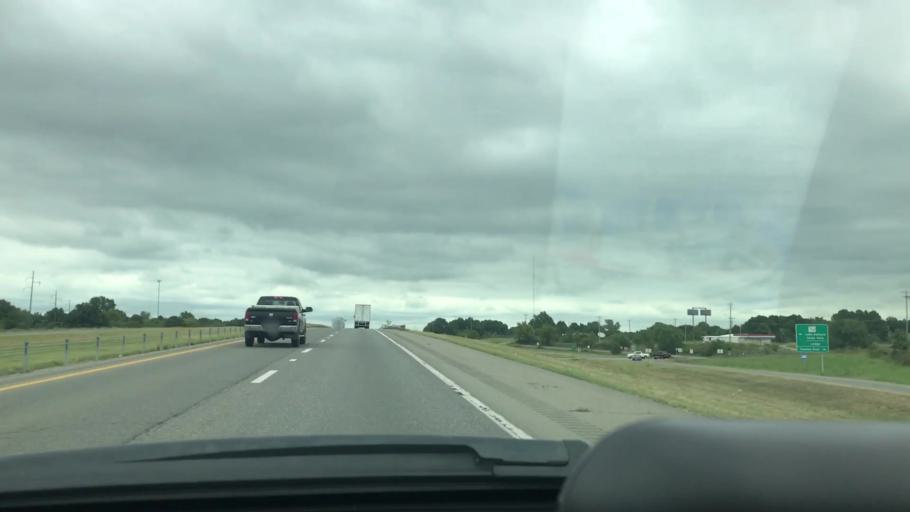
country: US
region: Oklahoma
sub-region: McIntosh County
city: Eufaula
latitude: 35.3603
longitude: -95.5746
